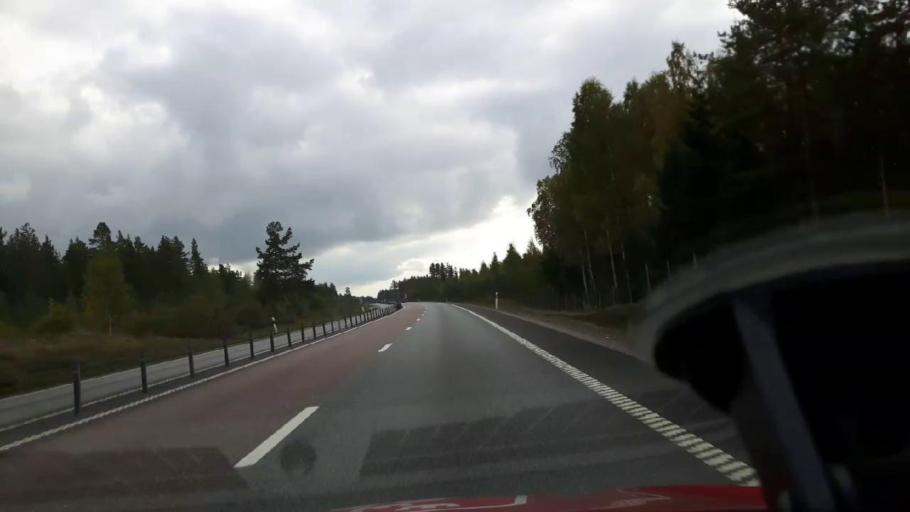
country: SE
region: Gaevleborg
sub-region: Gavle Kommun
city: Norrsundet
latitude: 61.0431
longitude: 16.9629
